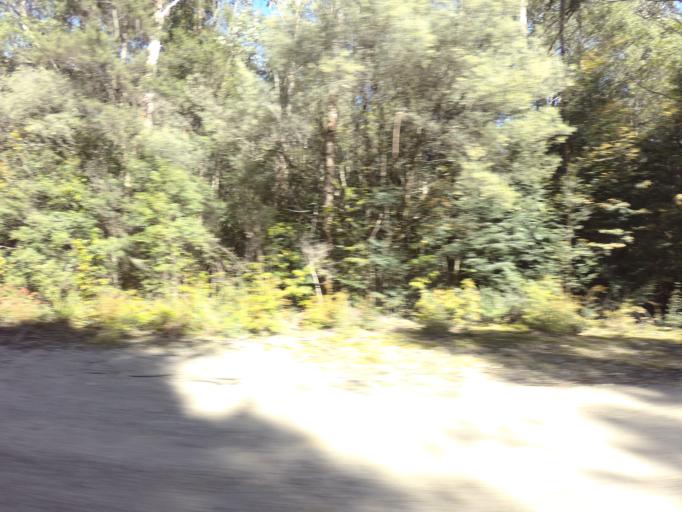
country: AU
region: Tasmania
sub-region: Huon Valley
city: Geeveston
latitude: -42.8660
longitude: 146.3678
